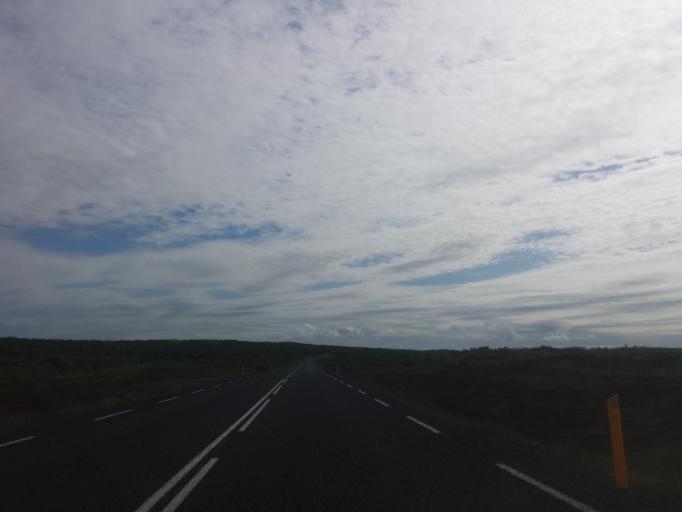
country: IS
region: Northeast
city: Husavik
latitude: 66.0157
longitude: -16.5723
